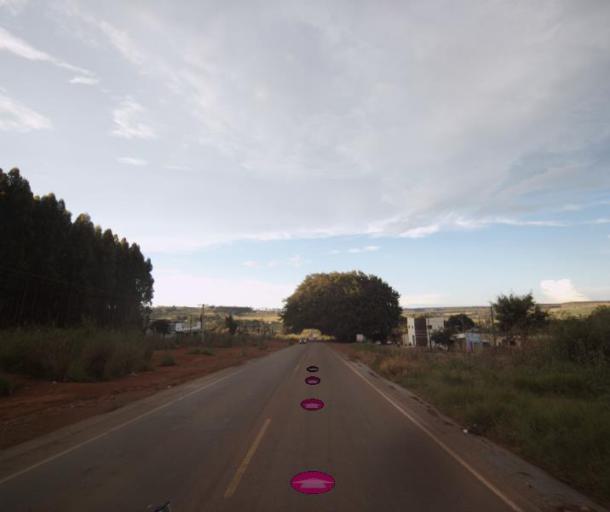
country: BR
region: Goias
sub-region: Anapolis
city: Anapolis
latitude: -16.2794
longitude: -48.9420
